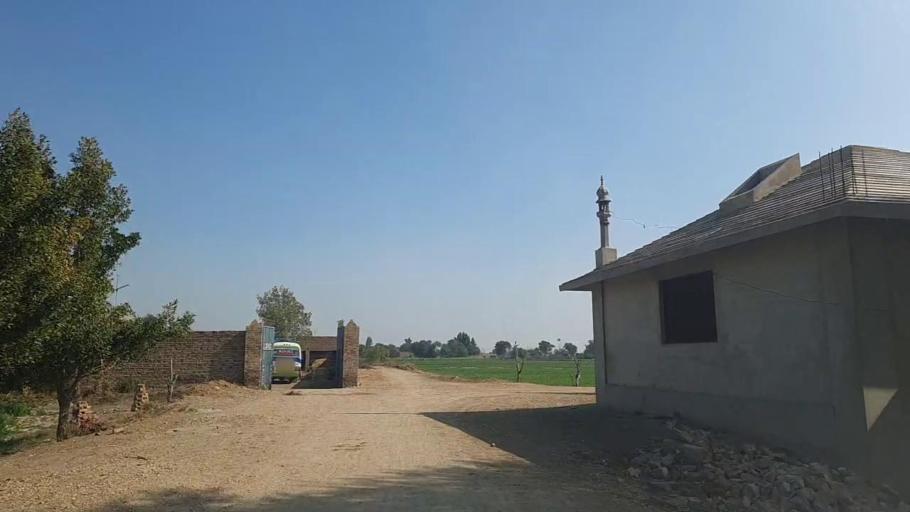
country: PK
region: Sindh
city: Shahpur Chakar
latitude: 26.1911
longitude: 68.6086
